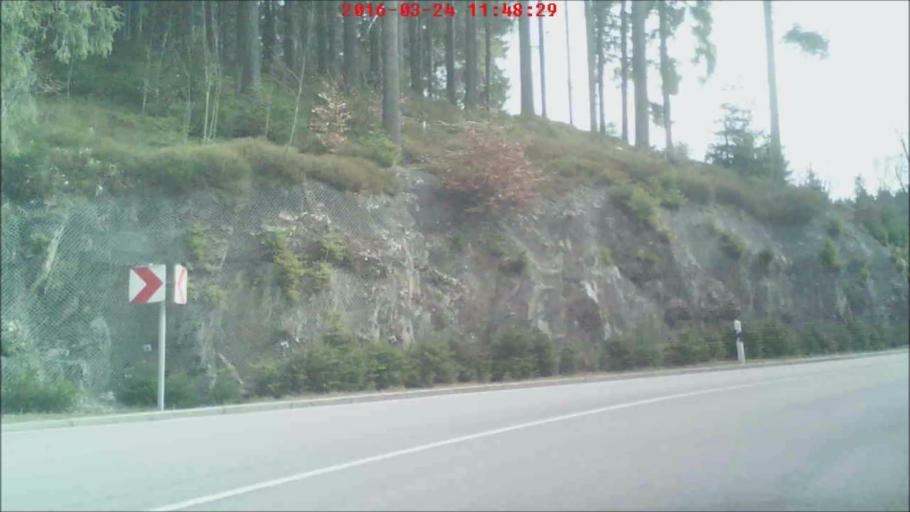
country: DE
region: Thuringia
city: Steinheid
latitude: 50.4642
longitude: 11.0292
